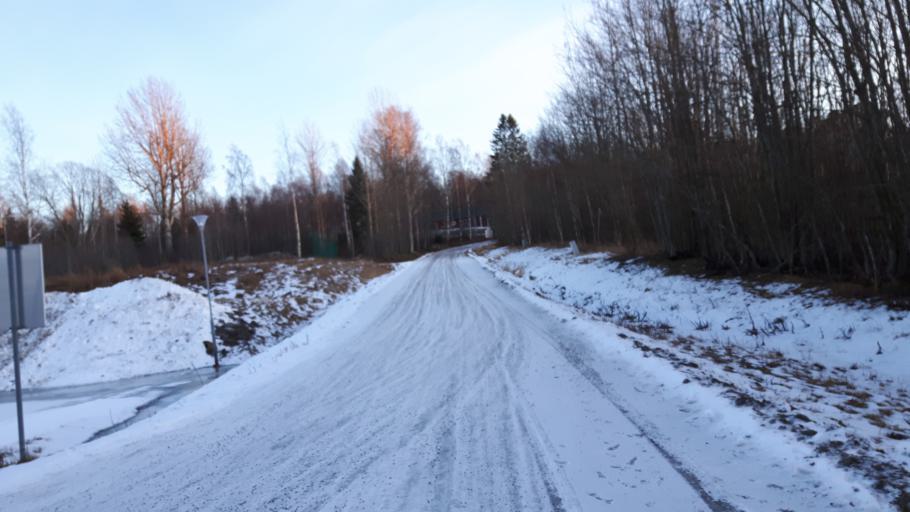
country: SE
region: Vaesternorrland
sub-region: Haernoesands Kommun
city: Haernoesand
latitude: 62.6204
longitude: 17.9360
